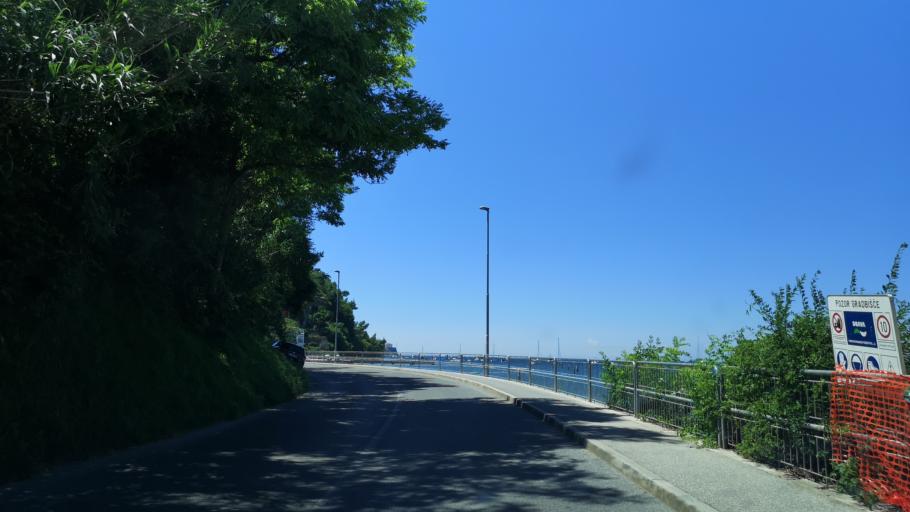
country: SI
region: Piran-Pirano
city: Portoroz
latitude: 45.5258
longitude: 13.6016
